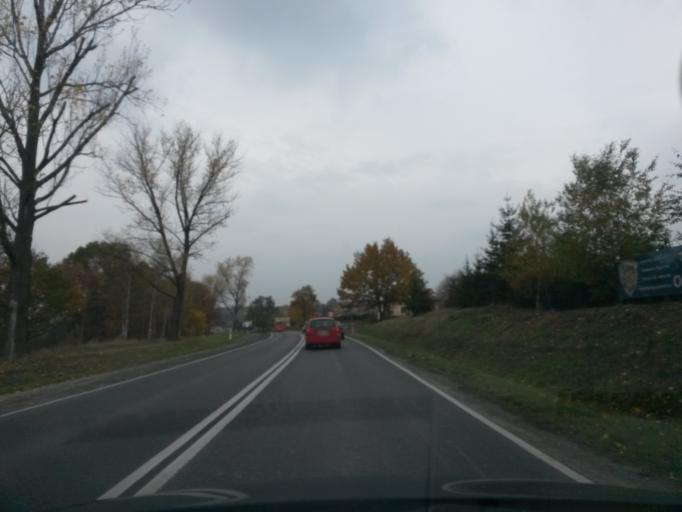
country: PL
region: Lower Silesian Voivodeship
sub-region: Powiat klodzki
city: Klodzko
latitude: 50.4168
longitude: 16.6602
